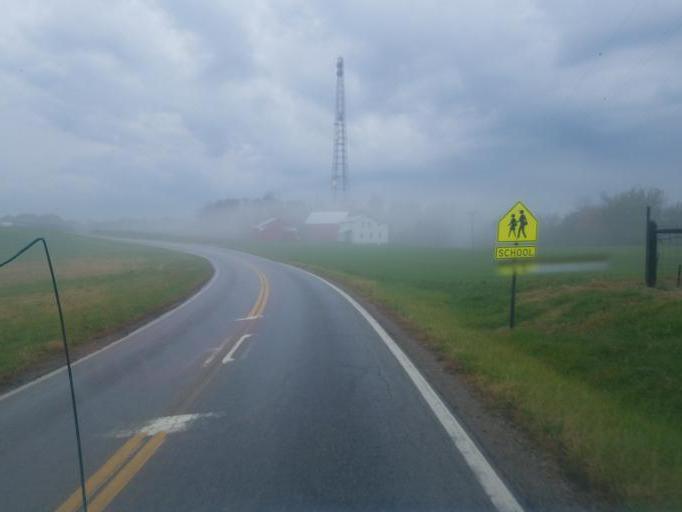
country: US
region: Ohio
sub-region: Morgan County
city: McConnelsville
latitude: 39.4928
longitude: -81.8842
